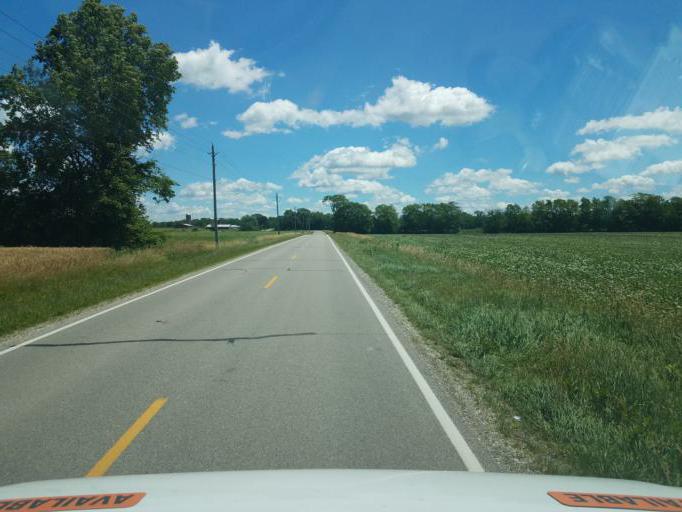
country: US
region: Ohio
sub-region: Crawford County
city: Galion
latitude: 40.7334
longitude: -82.8631
